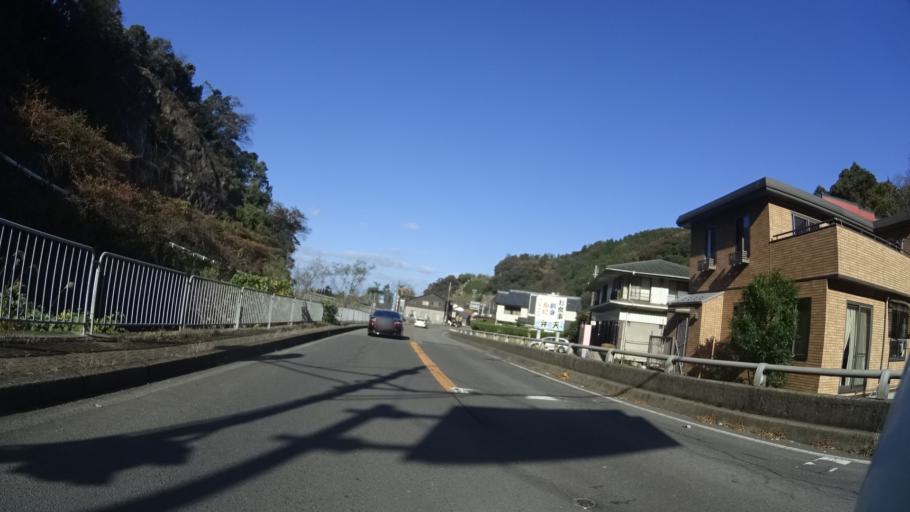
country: JP
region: Fukui
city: Takefu
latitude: 35.8214
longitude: 136.0737
